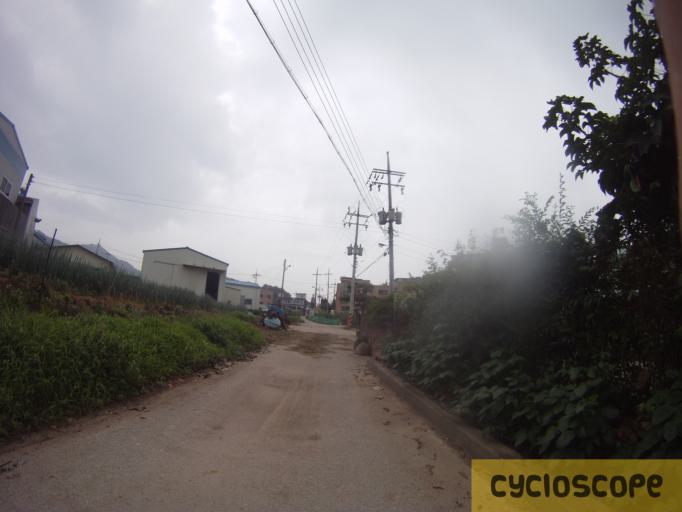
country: KR
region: Gyeonggi-do
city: Hwaseong-si
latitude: 37.1666
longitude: 126.9324
